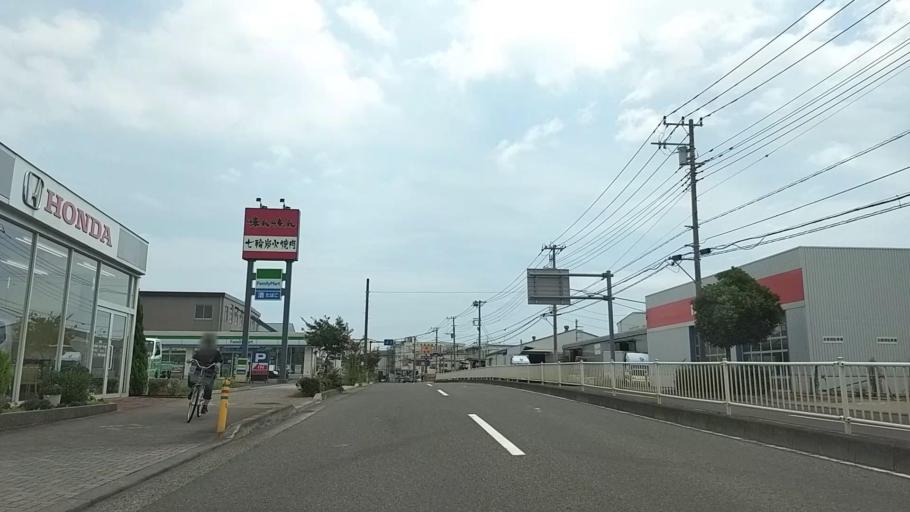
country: JP
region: Kanagawa
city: Minami-rinkan
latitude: 35.4539
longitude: 139.4176
